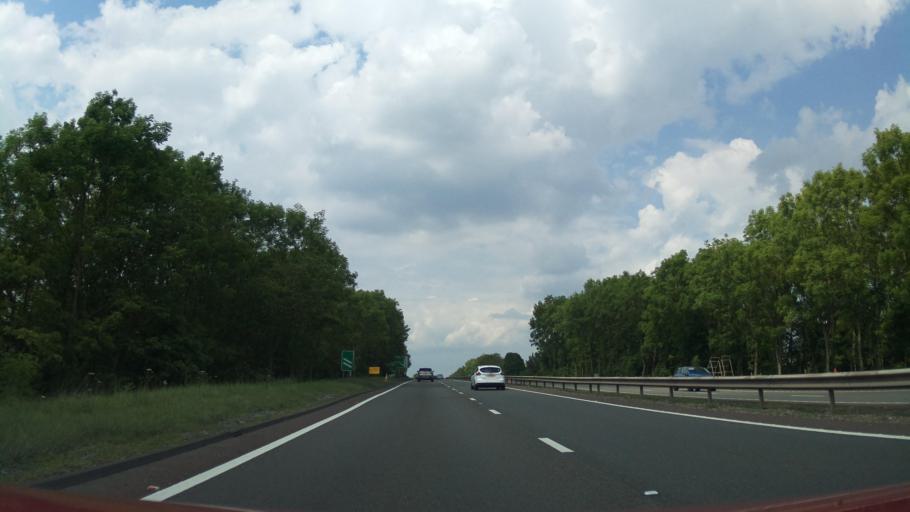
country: GB
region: England
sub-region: North Yorkshire
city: Thirsk
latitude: 54.2482
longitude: -1.3400
